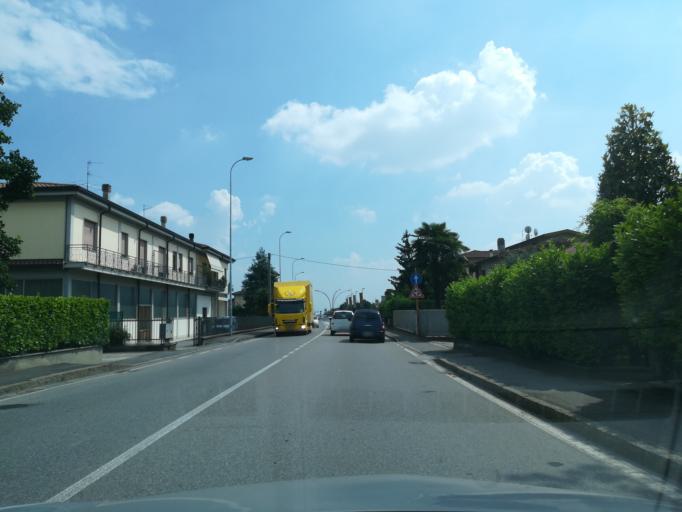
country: IT
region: Lombardy
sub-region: Provincia di Bergamo
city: Bolgare
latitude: 45.6362
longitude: 9.8080
